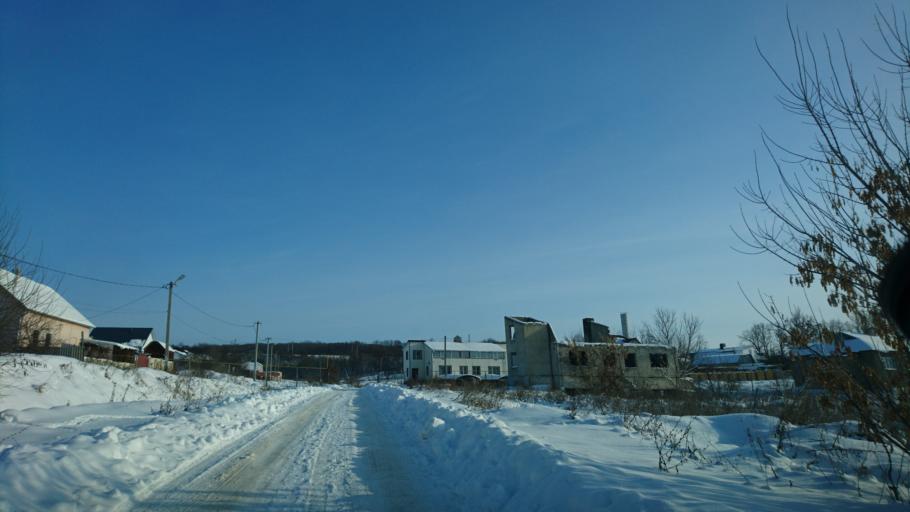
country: RU
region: Belgorod
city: Severnyy
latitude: 50.7221
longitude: 36.6100
